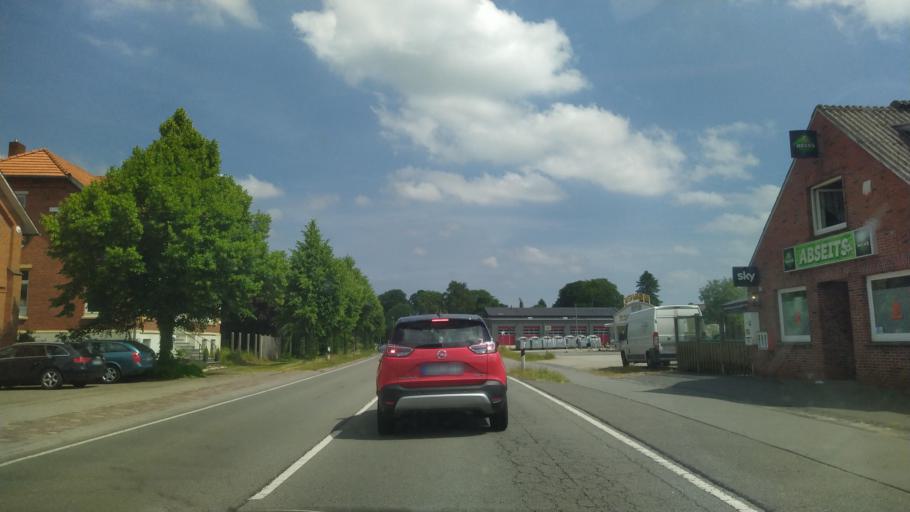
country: DE
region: Lower Saxony
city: Weener
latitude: 53.1672
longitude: 7.3430
